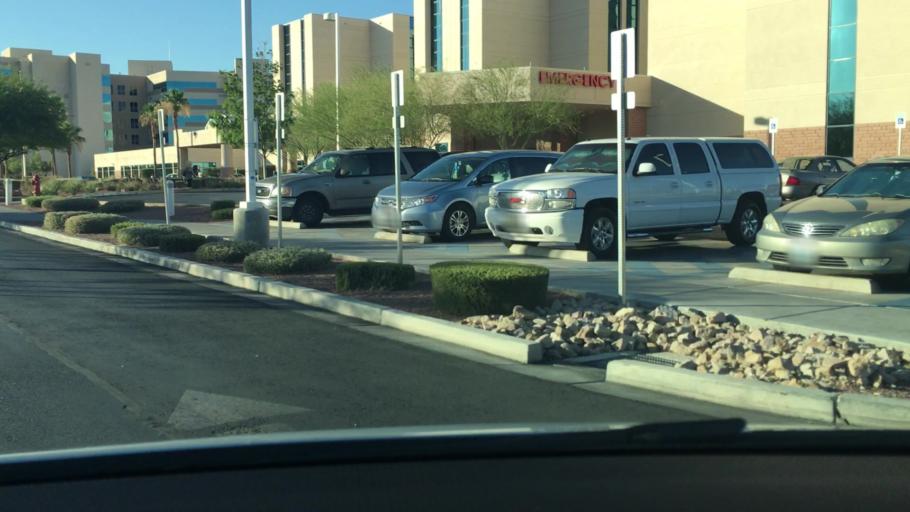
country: US
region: Nevada
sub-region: Clark County
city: Spring Valley
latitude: 36.2145
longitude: -115.2494
